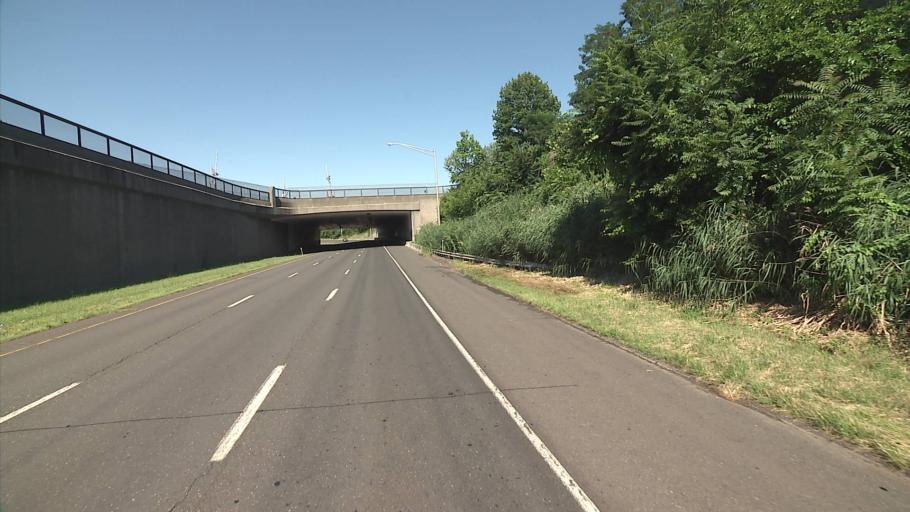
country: US
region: Connecticut
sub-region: Hartford County
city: New Britain
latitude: 41.6696
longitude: -72.7845
